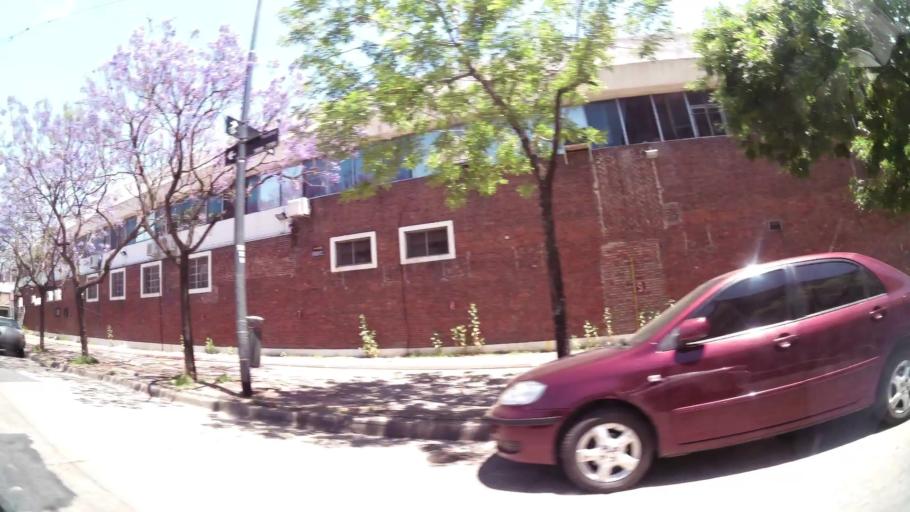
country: AR
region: Buenos Aires
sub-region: Partido de Avellaneda
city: Avellaneda
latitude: -34.6554
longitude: -58.3838
